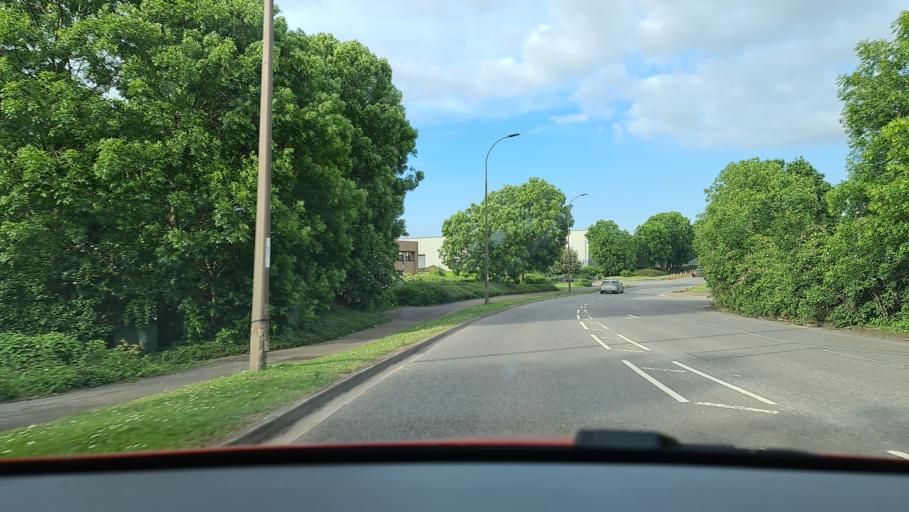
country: GB
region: England
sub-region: Peterborough
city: Castor
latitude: 52.5361
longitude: -0.3171
